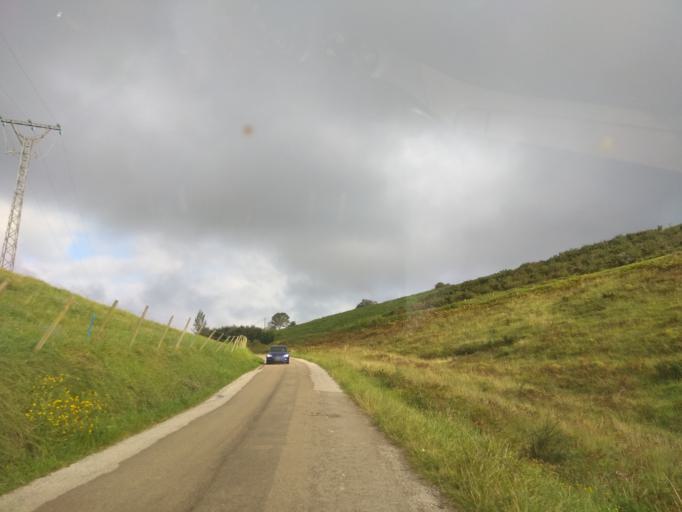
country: ES
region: Cantabria
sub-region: Provincia de Cantabria
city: San Vicente de la Barquera
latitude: 43.3128
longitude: -4.3835
